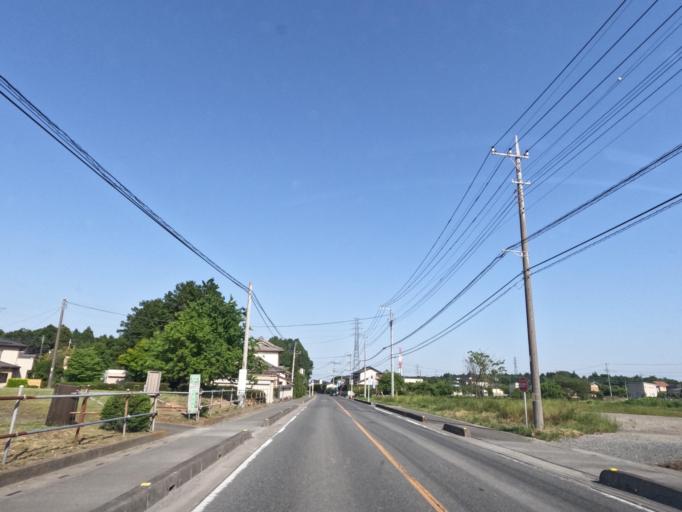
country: JP
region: Saitama
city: Ogawa
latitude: 36.1058
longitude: 139.2593
